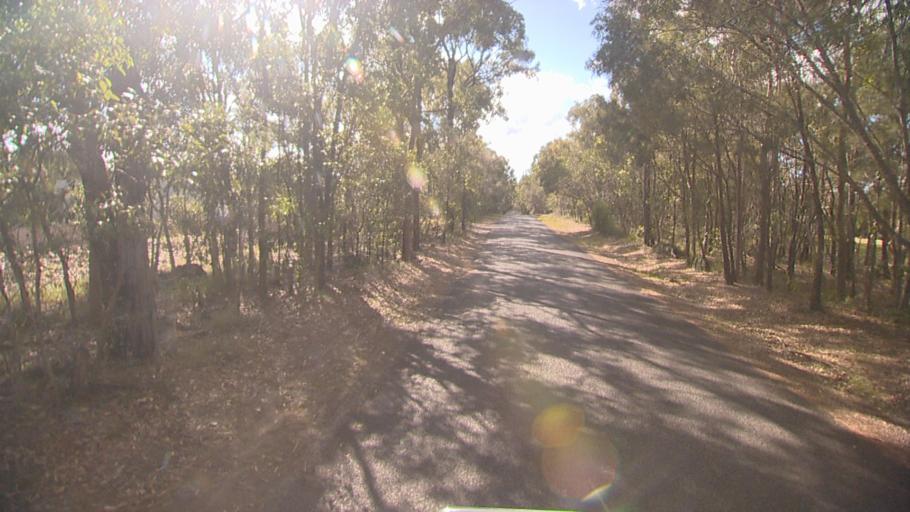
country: AU
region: Queensland
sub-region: Logan
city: Beenleigh
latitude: -27.6565
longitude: 153.2294
